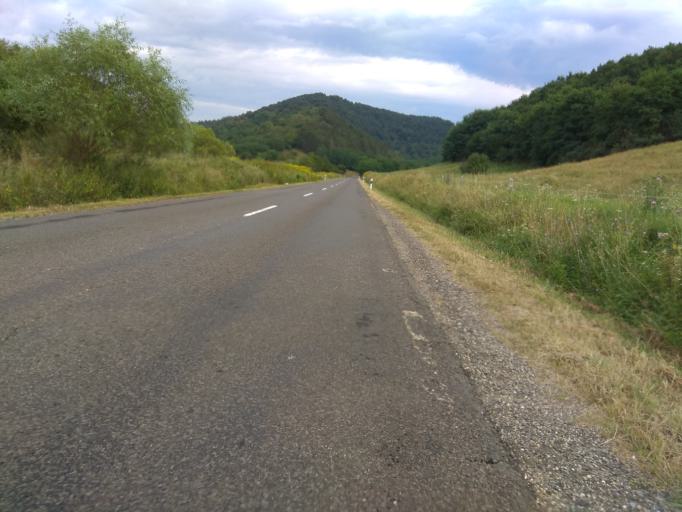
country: HU
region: Heves
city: Tarnalelesz
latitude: 48.0603
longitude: 20.2028
